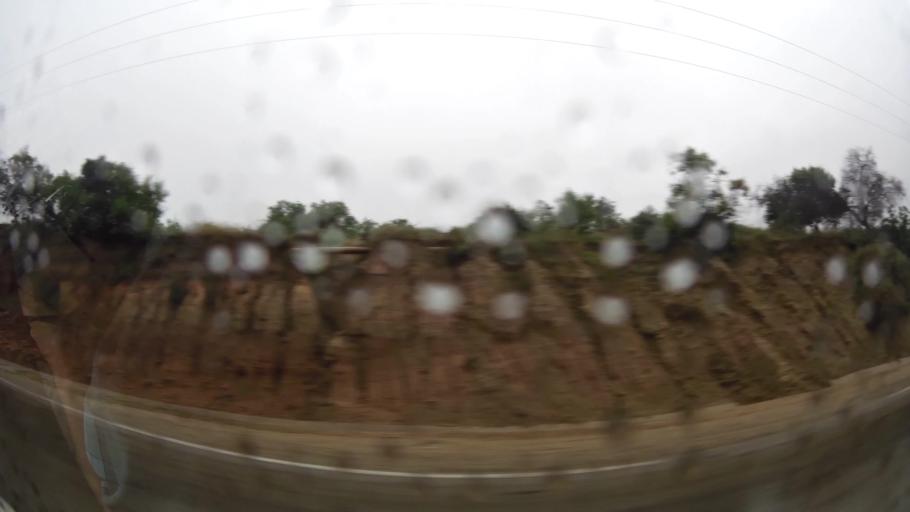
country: MA
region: Taza-Al Hoceima-Taounate
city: Tirhanimine
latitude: 35.2243
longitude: -3.9296
